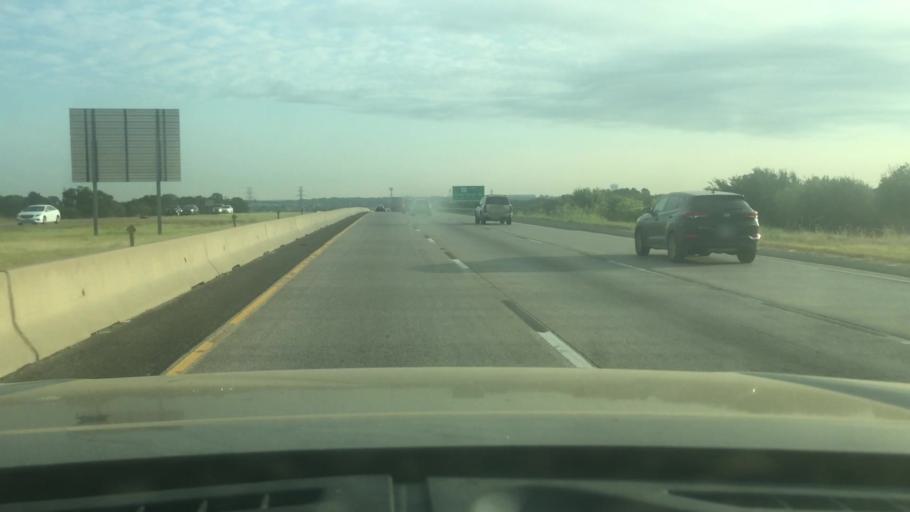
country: US
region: Texas
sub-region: Tarrant County
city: Euless
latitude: 32.8562
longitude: -97.1075
